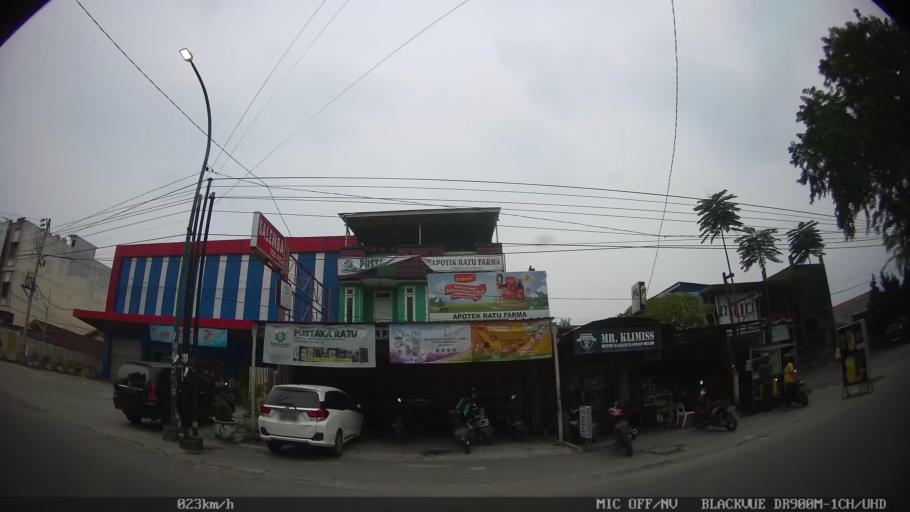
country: ID
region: North Sumatra
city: Medan
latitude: 3.5686
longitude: 98.6974
